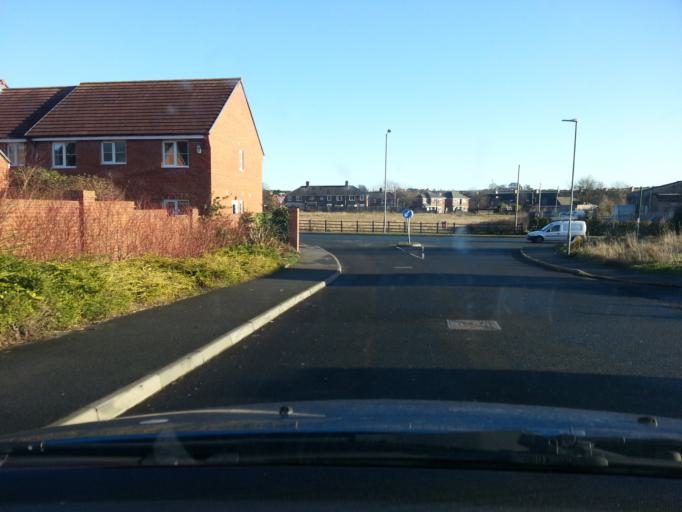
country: GB
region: England
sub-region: County Durham
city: Crook
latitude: 54.7099
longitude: -1.7527
